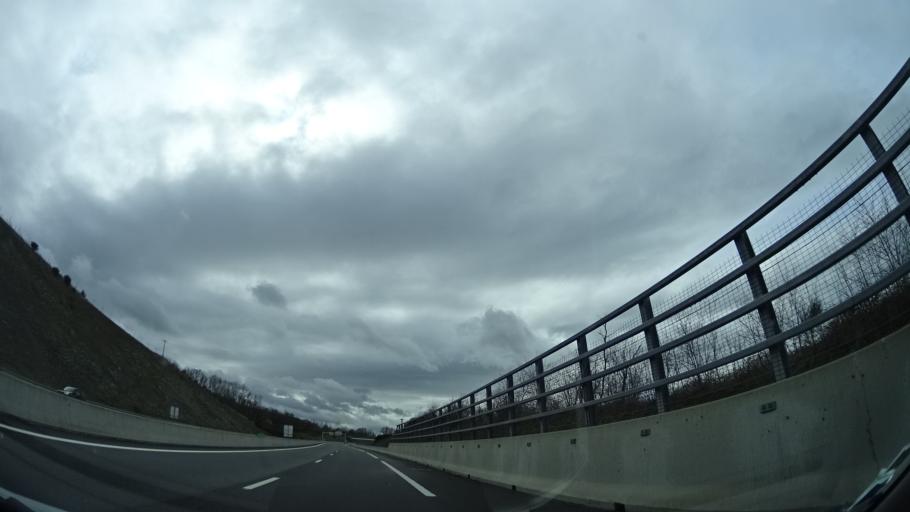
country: FR
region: Rhone-Alpes
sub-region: Departement du Rhone
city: Lentilly
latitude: 45.8522
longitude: 4.6507
